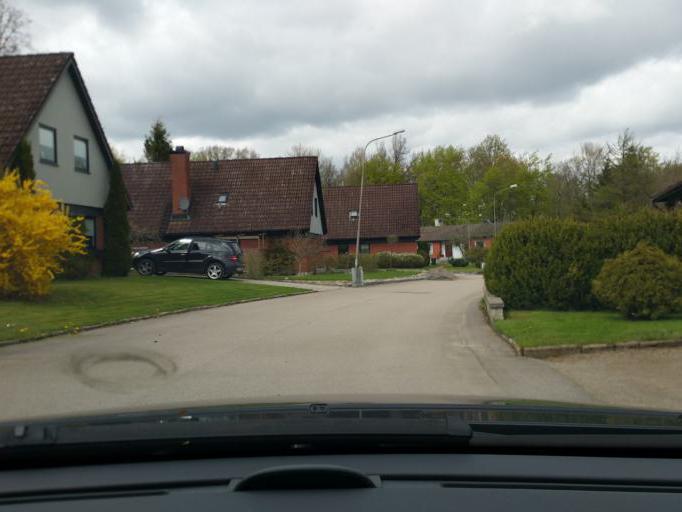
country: SE
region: Kronoberg
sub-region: Vaxjo Kommun
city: Lammhult
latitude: 57.1731
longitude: 14.5710
